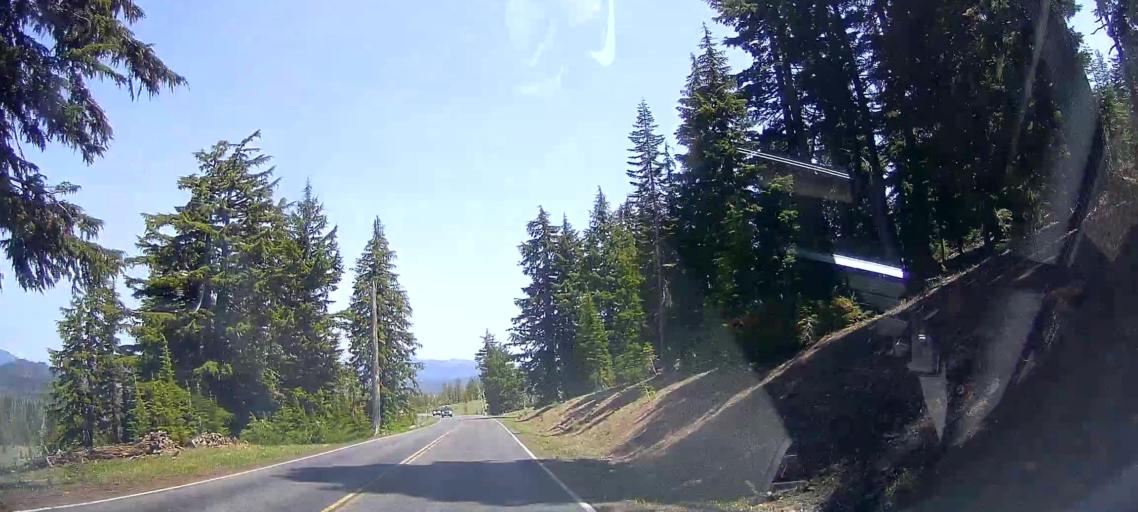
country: US
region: Oregon
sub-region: Jackson County
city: Shady Cove
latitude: 42.9877
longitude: -122.1448
